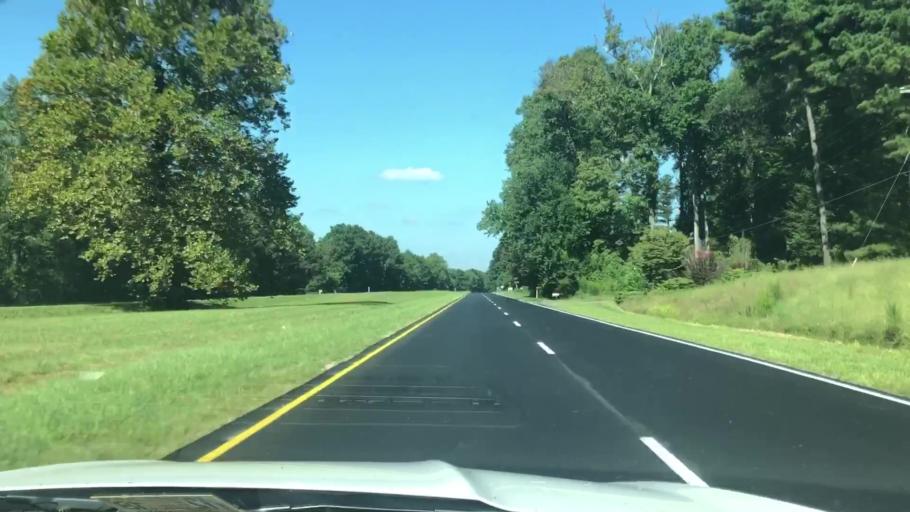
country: US
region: Virginia
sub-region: New Kent County
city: New Kent
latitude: 37.4374
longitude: -77.0173
